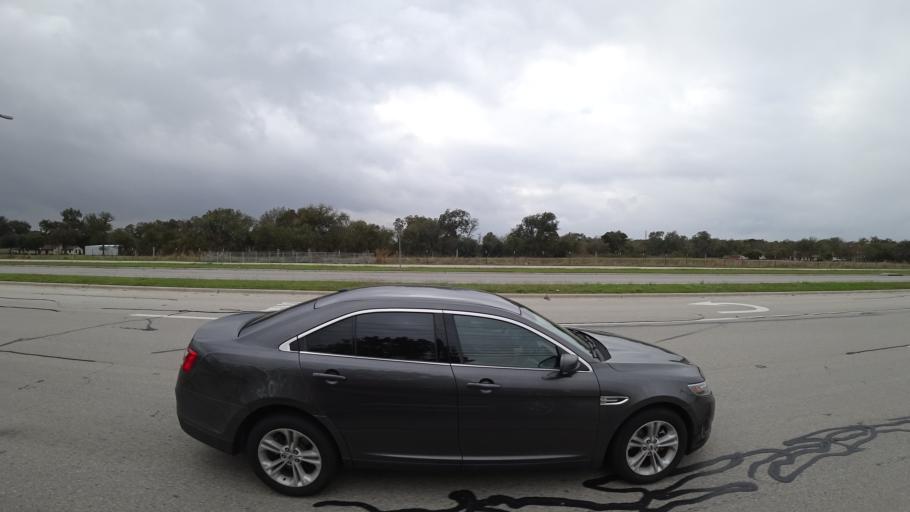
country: US
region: Texas
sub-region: Travis County
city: Pflugerville
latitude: 30.4307
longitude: -97.6014
